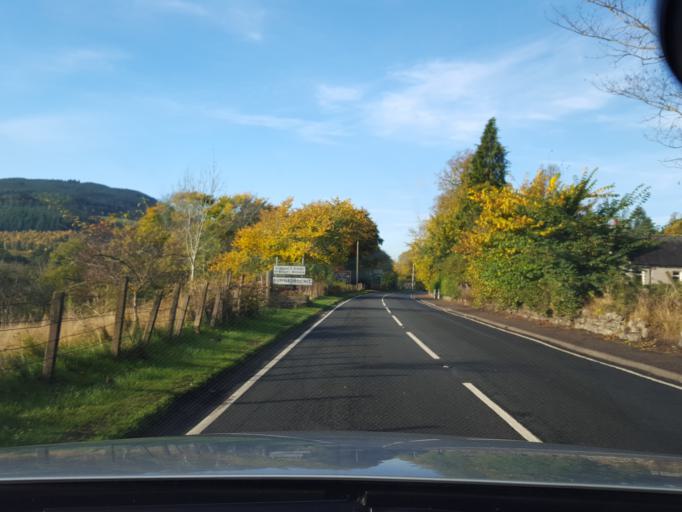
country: GB
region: Scotland
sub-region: Highland
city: Beauly
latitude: 57.3371
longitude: -4.4747
